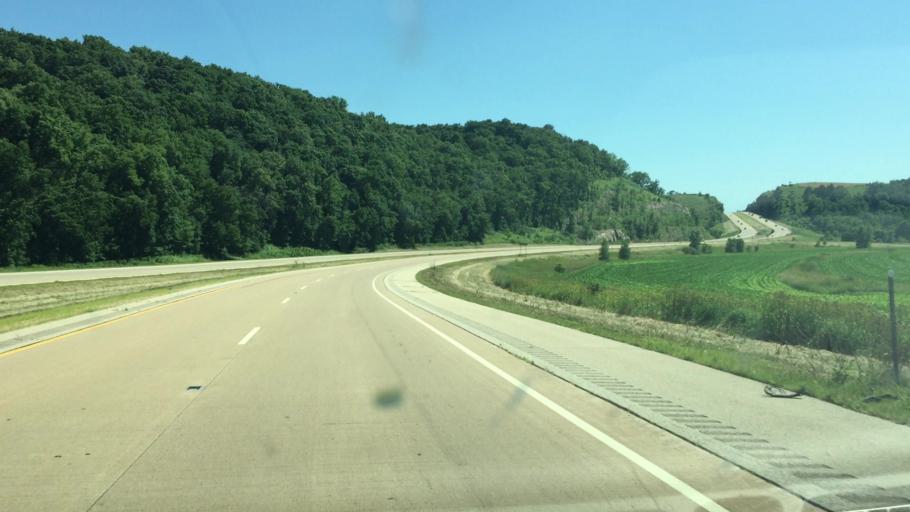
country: US
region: Wisconsin
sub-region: Grant County
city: Dickeyville
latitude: 42.6510
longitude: -90.5743
